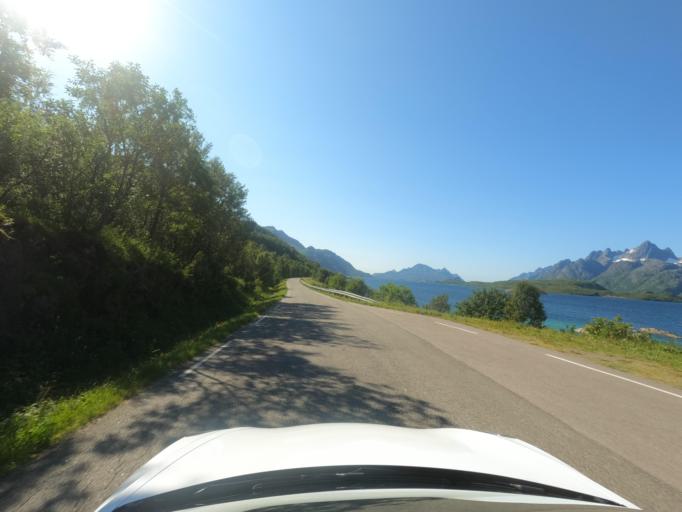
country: NO
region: Nordland
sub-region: Hadsel
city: Stokmarknes
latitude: 68.3738
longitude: 15.0770
